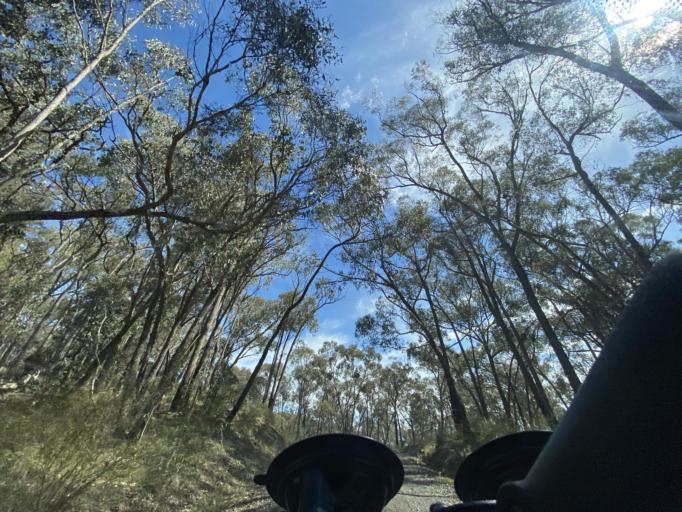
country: AU
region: Victoria
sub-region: Mansfield
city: Mansfield
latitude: -36.8004
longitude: 146.1113
